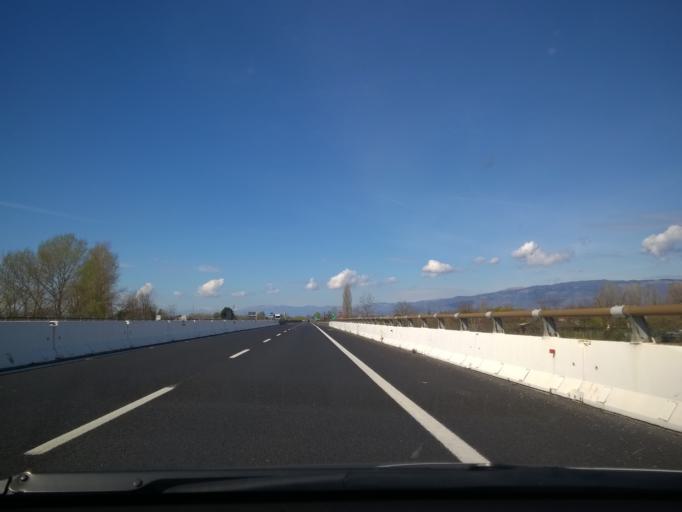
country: IT
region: Friuli Venezia Giulia
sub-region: Provincia di Pordenone
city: Pordenone
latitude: 45.9445
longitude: 12.6376
